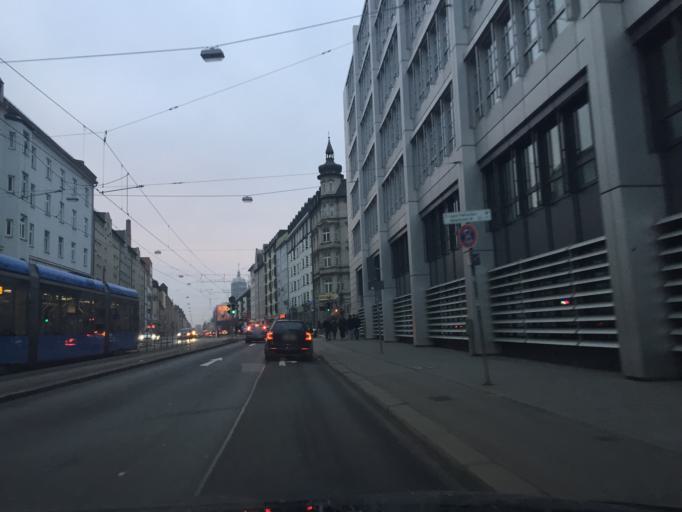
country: DE
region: Bavaria
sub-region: Upper Bavaria
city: Munich
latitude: 48.1392
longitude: 11.5481
